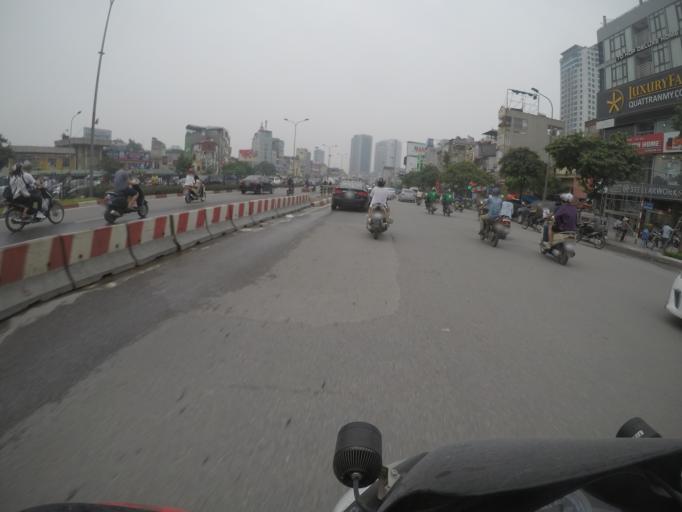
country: VN
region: Ha Noi
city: Thanh Xuan
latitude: 21.0018
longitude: 105.8186
